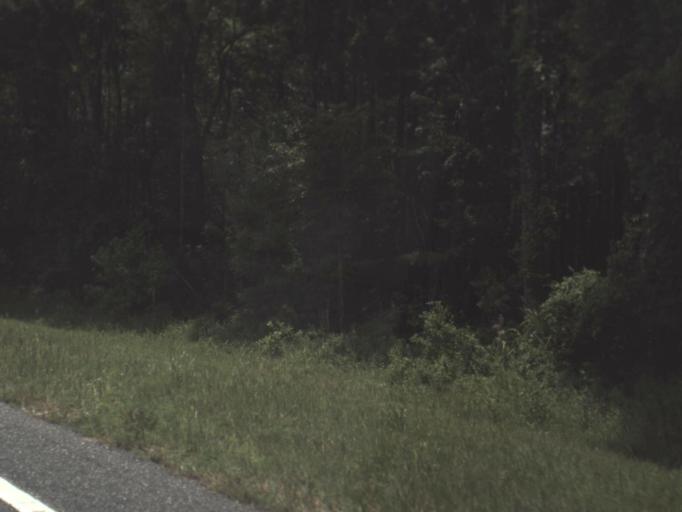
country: US
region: Florida
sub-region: Taylor County
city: Steinhatchee
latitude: 29.8793
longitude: -83.4076
